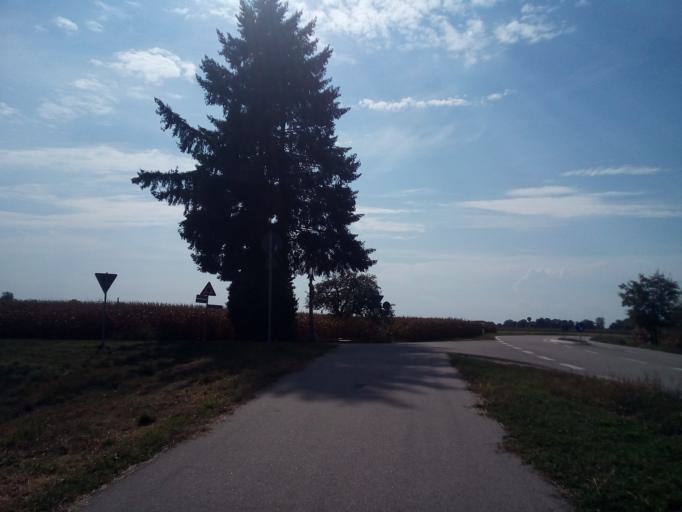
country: DE
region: Baden-Wuerttemberg
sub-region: Karlsruhe Region
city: Zell
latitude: 48.6855
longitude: 8.0503
